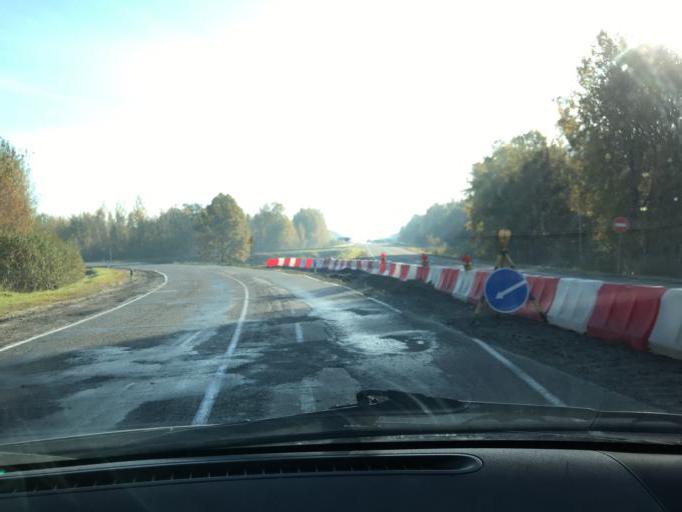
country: BY
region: Brest
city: Horad Luninyets
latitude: 52.2819
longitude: 26.8202
